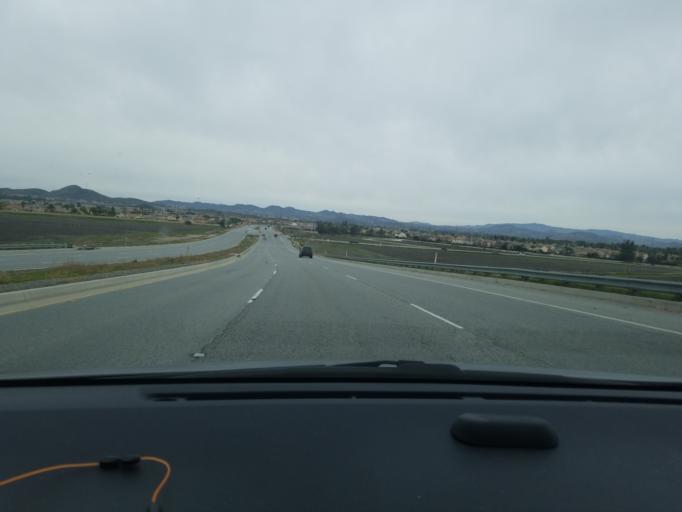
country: US
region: California
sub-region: Riverside County
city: Menifee
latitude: 33.6930
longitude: -117.1403
